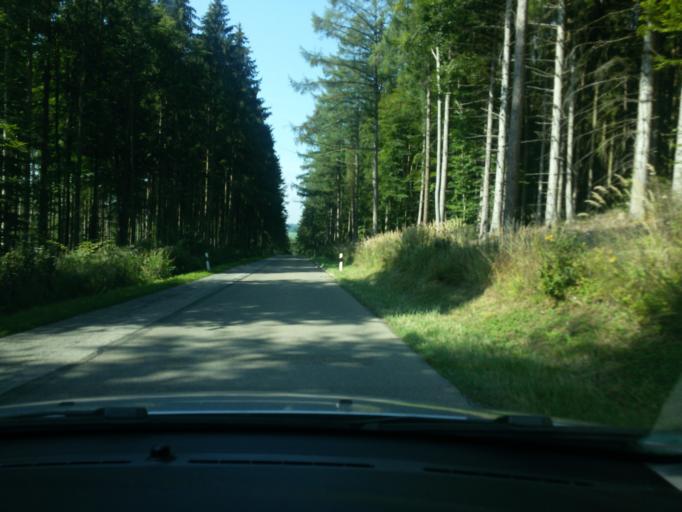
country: DE
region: Bavaria
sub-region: Swabia
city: Scherstetten
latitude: 48.1836
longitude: 10.6594
